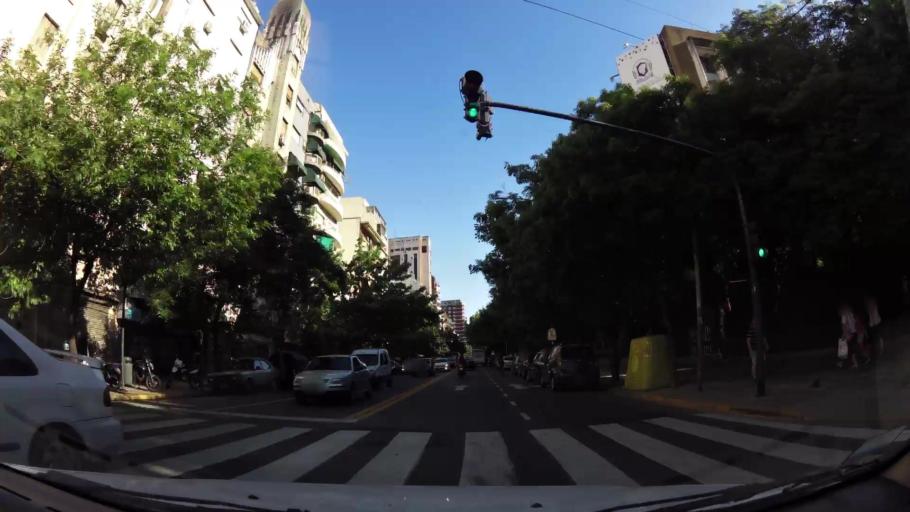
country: AR
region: Buenos Aires F.D.
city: Villa Santa Rita
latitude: -34.6195
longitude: -58.4358
